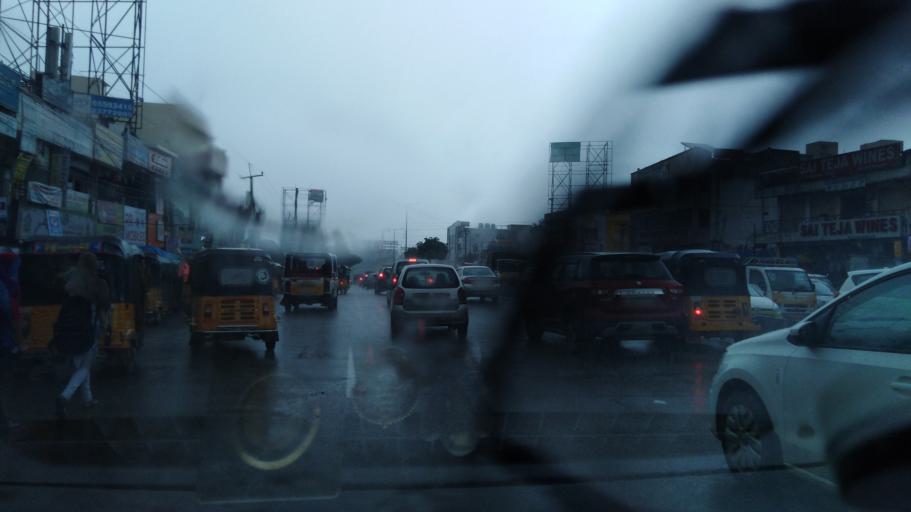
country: IN
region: Telangana
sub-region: Rangareddi
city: Kukatpalli
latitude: 17.4971
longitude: 78.3615
